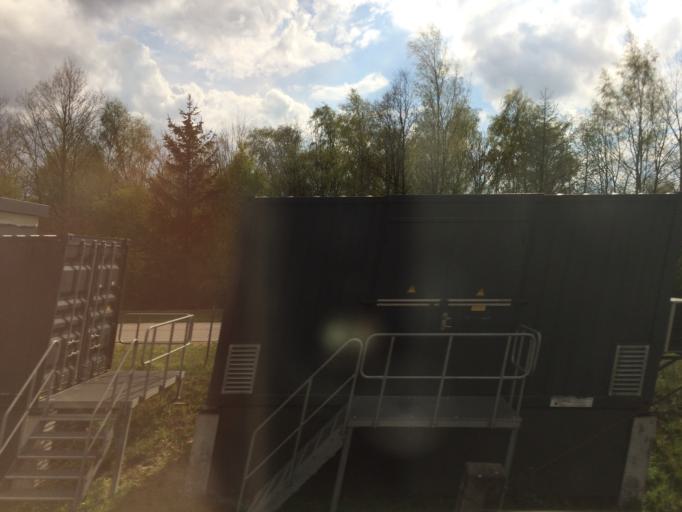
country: DK
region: South Denmark
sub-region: Nyborg Kommune
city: Nyborg
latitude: 55.3041
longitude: 10.8232
